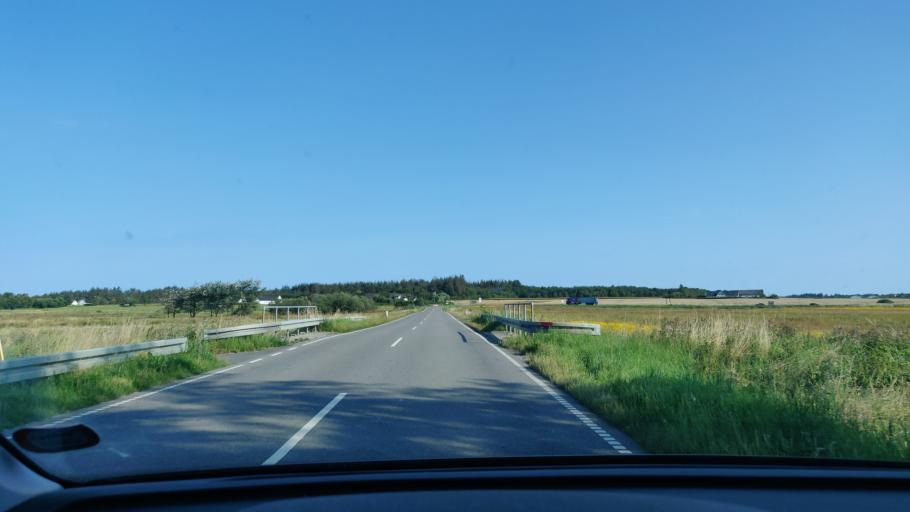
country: DK
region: North Denmark
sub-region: Jammerbugt Kommune
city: Pandrup
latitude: 57.2424
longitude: 9.6477
